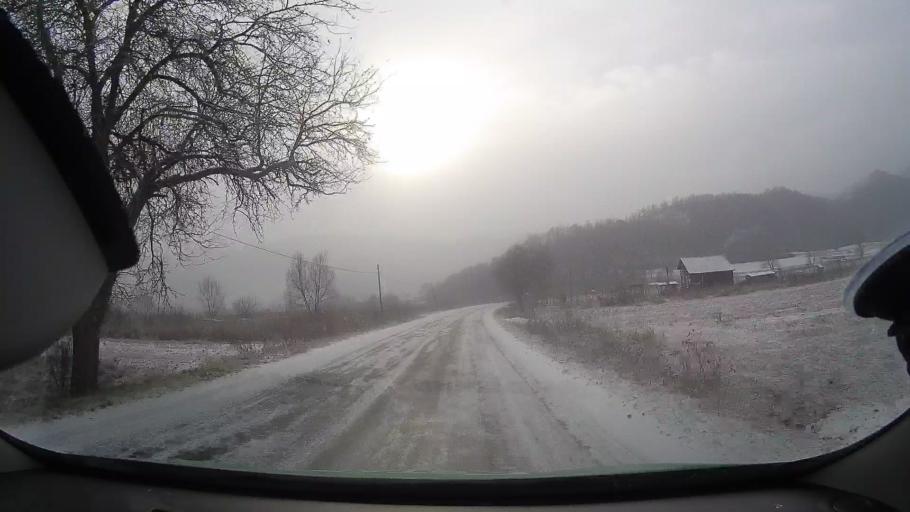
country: RO
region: Alba
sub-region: Comuna Rimetea
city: Rimetea
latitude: 46.3957
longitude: 23.5603
